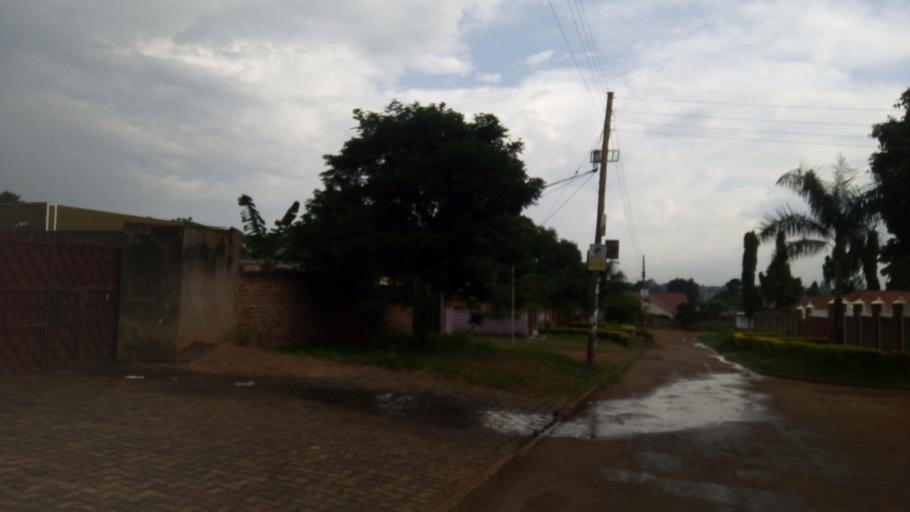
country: UG
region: Eastern Region
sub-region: Mbale District
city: Mbale
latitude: 1.0776
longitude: 34.1720
